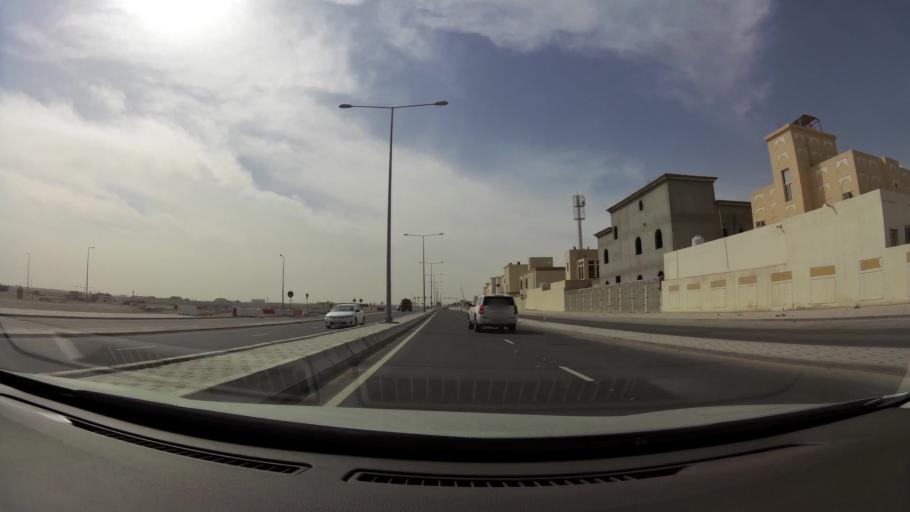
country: QA
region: Baladiyat ar Rayyan
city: Ar Rayyan
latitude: 25.3272
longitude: 51.3802
